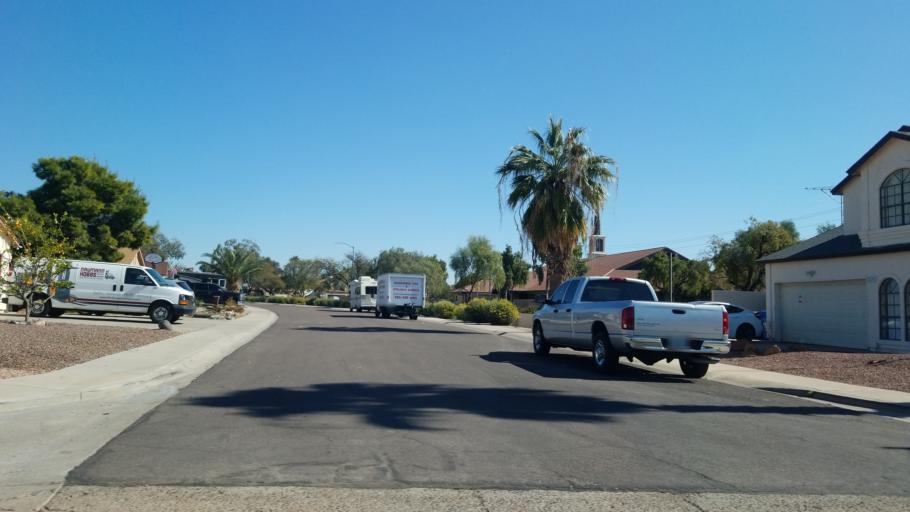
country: US
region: Arizona
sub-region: Maricopa County
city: Glendale
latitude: 33.6482
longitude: -112.0785
